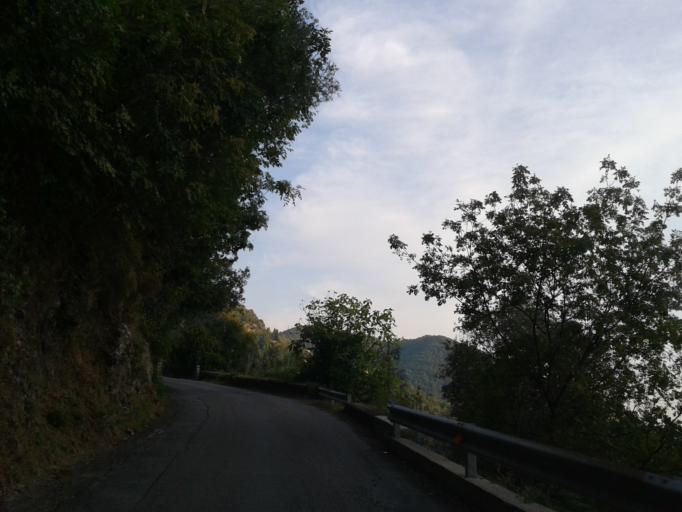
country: IT
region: Tuscany
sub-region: Provincia di Lucca
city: Pontestazzemese
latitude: 43.9603
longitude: 10.3238
